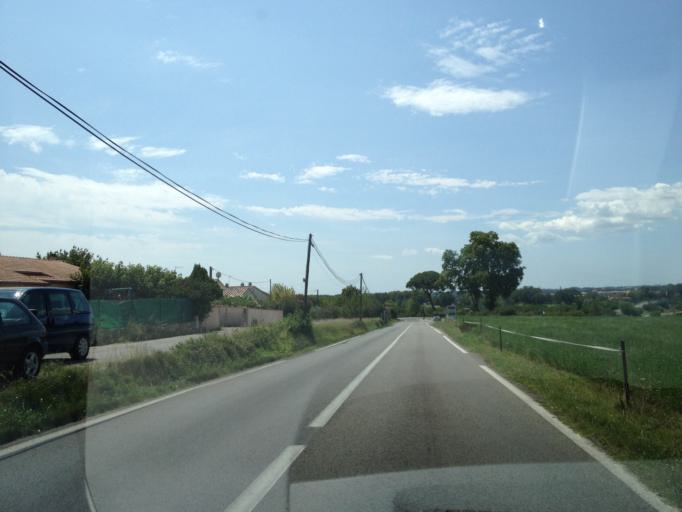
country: FR
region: Languedoc-Roussillon
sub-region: Departement du Gard
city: Sommieres
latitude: 43.7956
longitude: 4.0859
